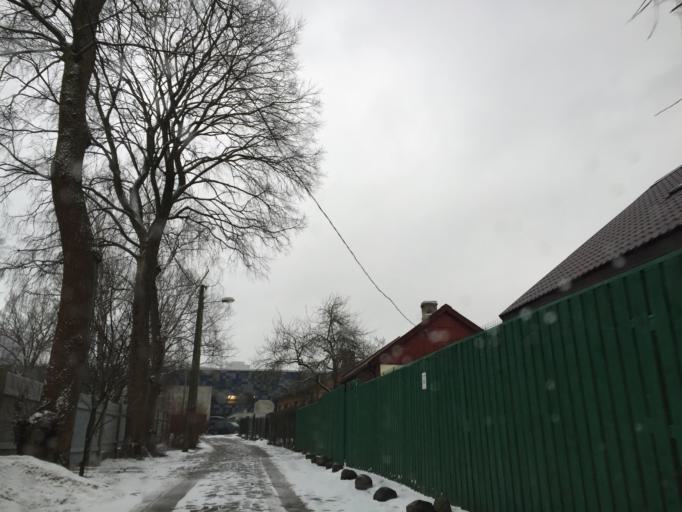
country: LV
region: Riga
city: Riga
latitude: 56.9536
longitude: 24.0845
